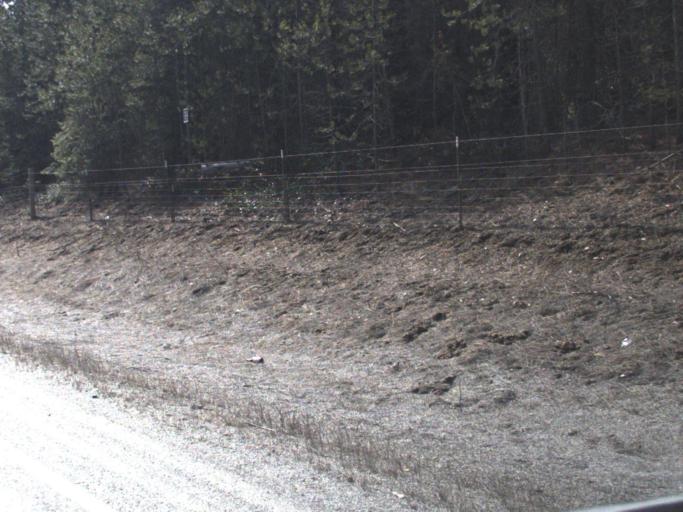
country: US
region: Washington
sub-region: Stevens County
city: Chewelah
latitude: 48.6429
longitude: -117.3748
